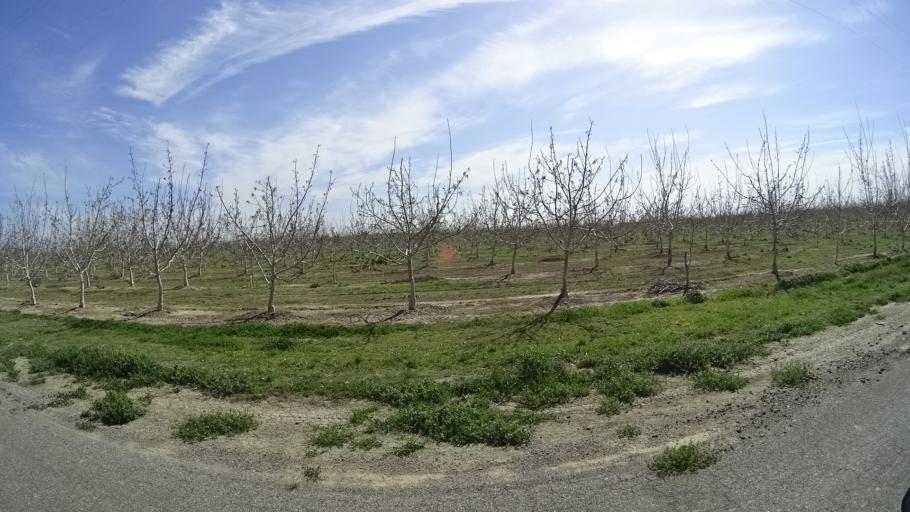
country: US
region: California
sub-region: Glenn County
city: Hamilton City
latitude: 39.6321
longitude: -122.0181
